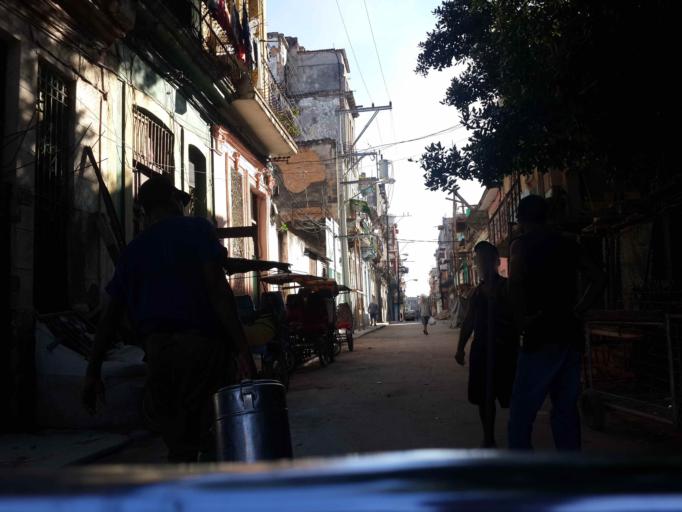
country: CU
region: La Habana
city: La Habana Vieja
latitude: 23.1299
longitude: -82.3585
